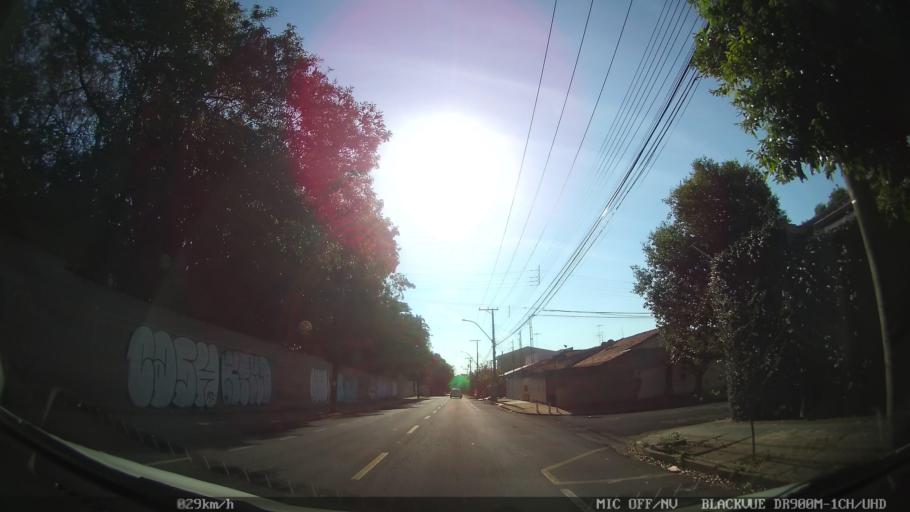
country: BR
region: Sao Paulo
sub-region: Sao Jose Do Rio Preto
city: Sao Jose do Rio Preto
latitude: -20.7828
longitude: -49.3592
